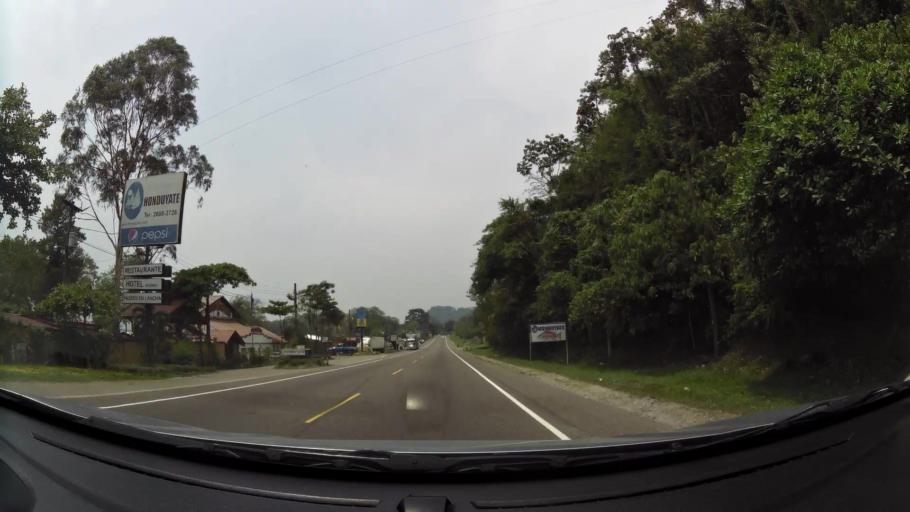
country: HN
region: Cortes
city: La Guama
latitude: 14.8577
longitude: -87.9538
